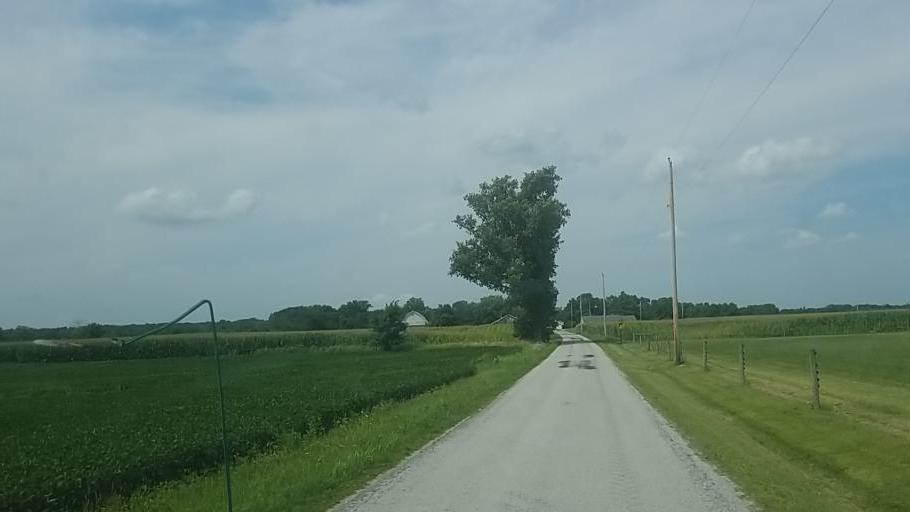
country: US
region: Ohio
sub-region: Hardin County
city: Forest
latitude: 40.7867
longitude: -83.5606
